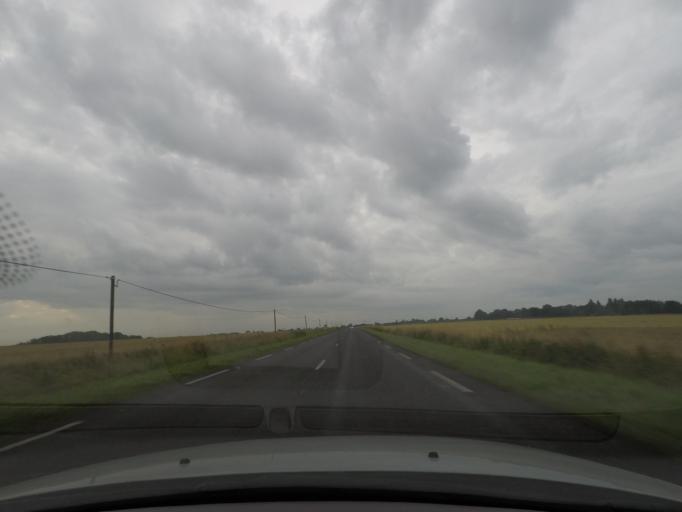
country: FR
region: Haute-Normandie
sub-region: Departement de la Seine-Maritime
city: Neufchatel-en-Bray
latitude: 49.7372
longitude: 1.4928
